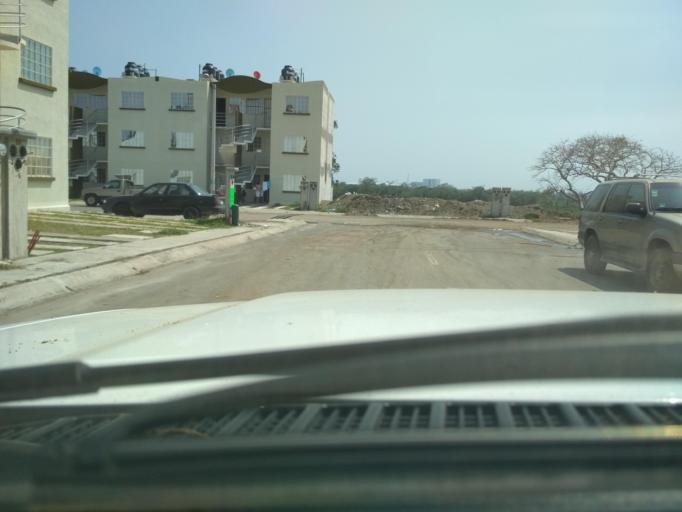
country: MX
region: Veracruz
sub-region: Veracruz
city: Lomas de Rio Medio Cuatro
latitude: 19.1840
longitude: -96.2090
